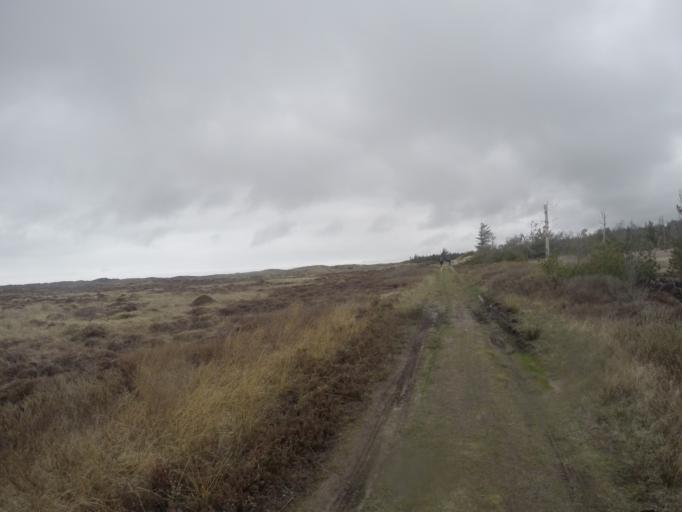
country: DK
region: North Denmark
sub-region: Thisted Kommune
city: Hurup
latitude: 56.9077
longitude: 8.3469
